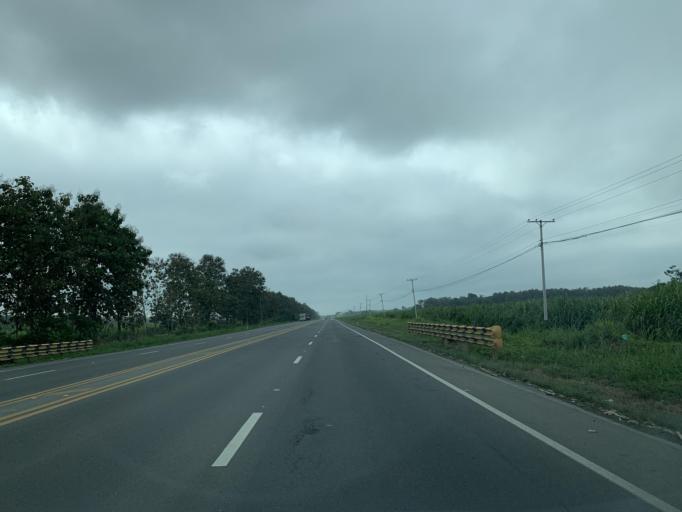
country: EC
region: Guayas
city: Coronel Marcelino Mariduena
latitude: -2.3081
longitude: -79.4800
